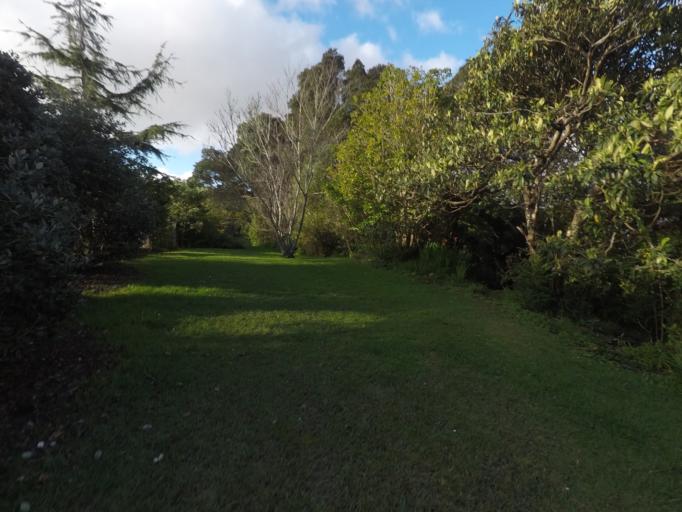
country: NZ
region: Auckland
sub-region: Auckland
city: Rosebank
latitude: -36.8983
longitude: 174.6713
